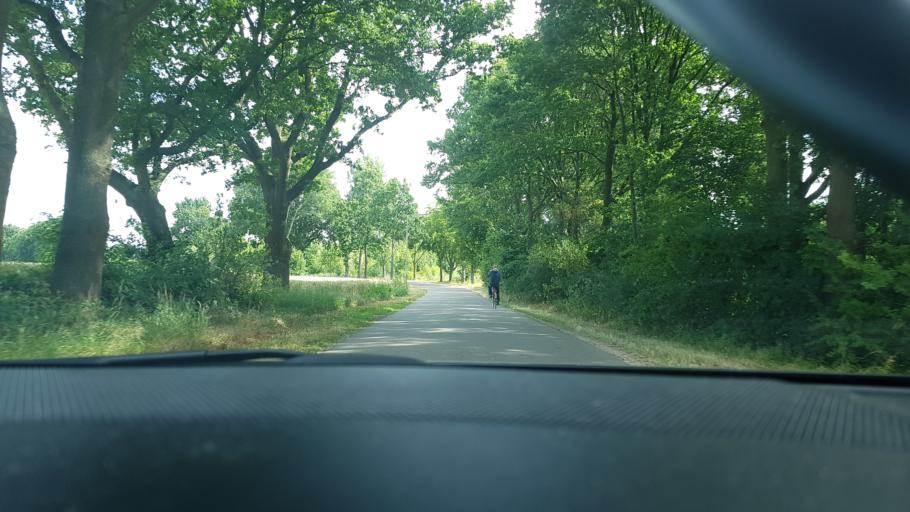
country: NL
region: Limburg
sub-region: Gemeente Roermond
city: Leeuwen
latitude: 51.2154
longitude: 6.0173
